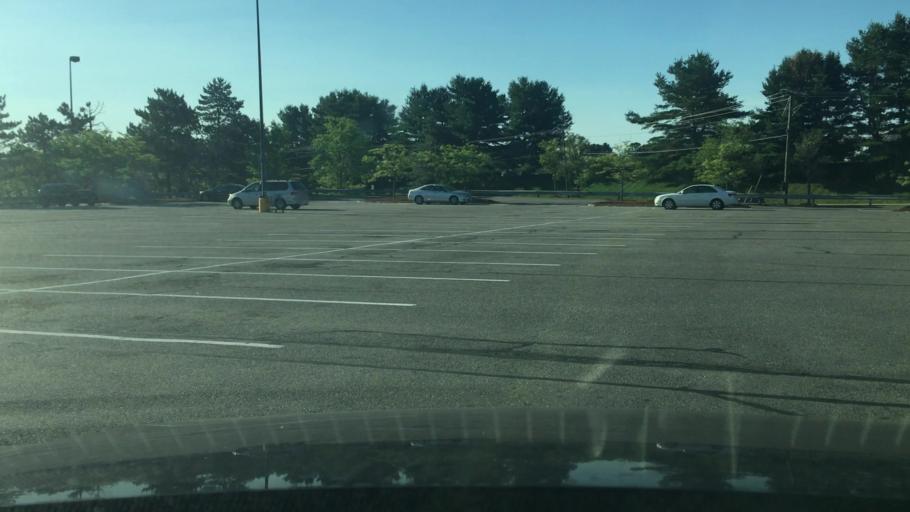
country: US
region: Massachusetts
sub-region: Essex County
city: Methuen
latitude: 42.7429
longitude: -71.1644
